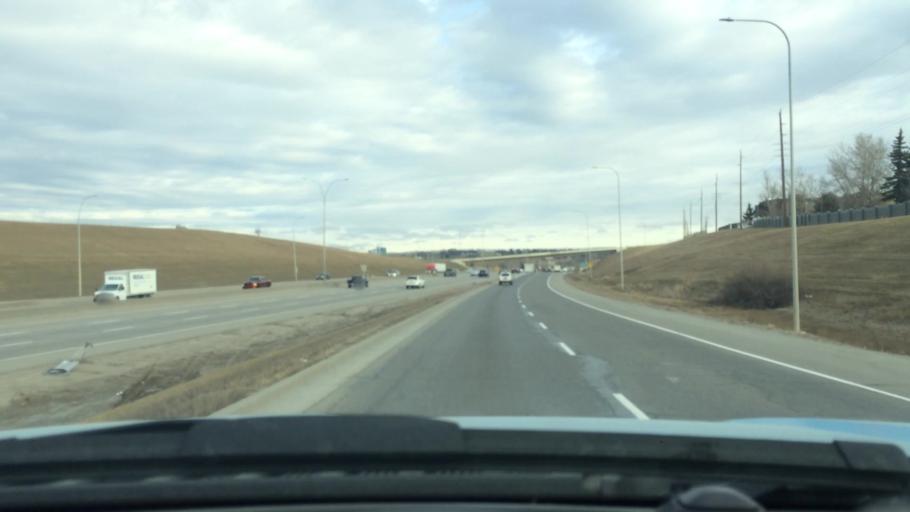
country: CA
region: Alberta
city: Calgary
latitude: 51.0195
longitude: -114.0024
